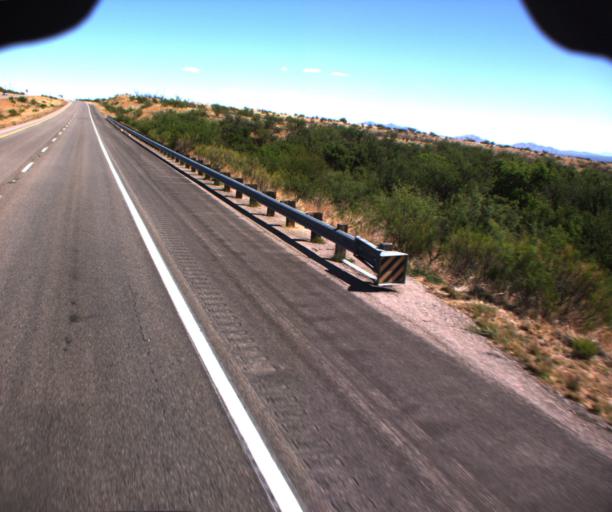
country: US
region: Arizona
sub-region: Cochise County
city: Whetstone
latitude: 31.8396
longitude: -110.3425
